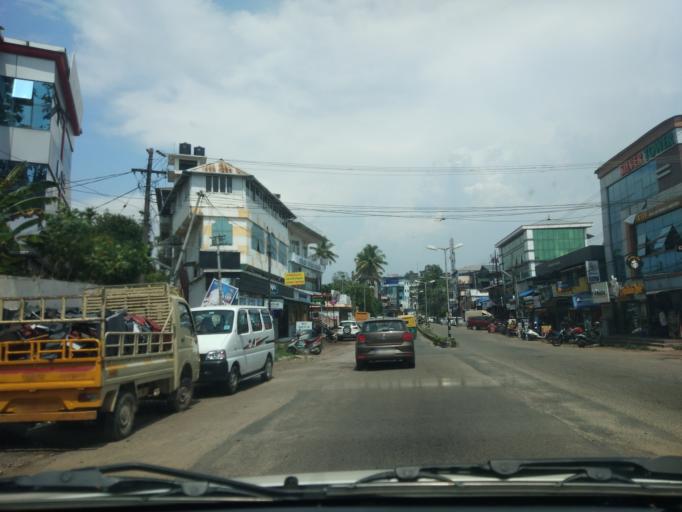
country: IN
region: Kerala
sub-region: Ernakulam
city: Elur
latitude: 10.0467
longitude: 76.3209
